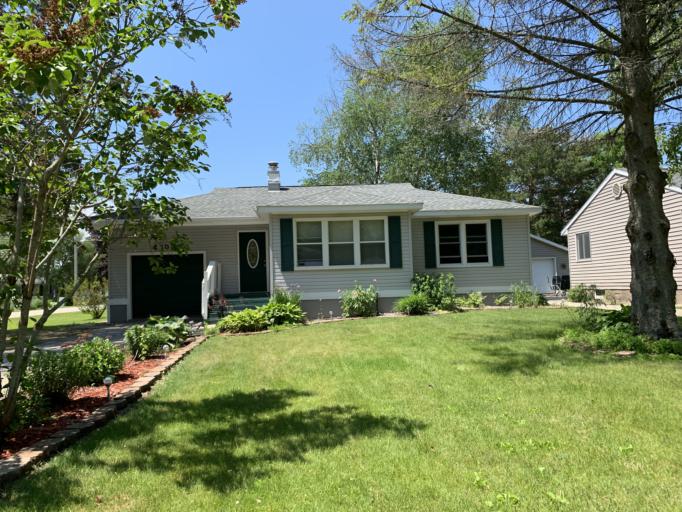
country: US
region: Michigan
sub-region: Menominee County
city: Menominee
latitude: 45.1396
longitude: -87.6078
